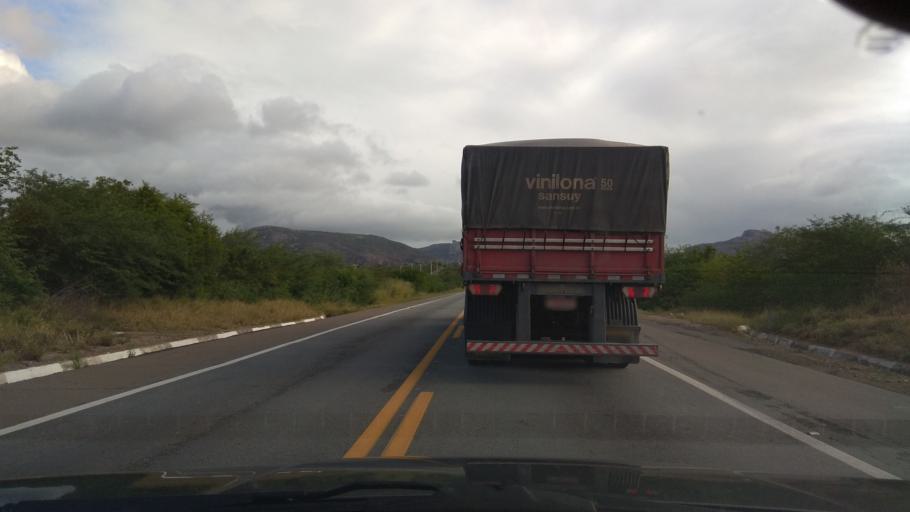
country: BR
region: Bahia
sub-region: Amargosa
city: Amargosa
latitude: -12.8314
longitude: -39.8301
